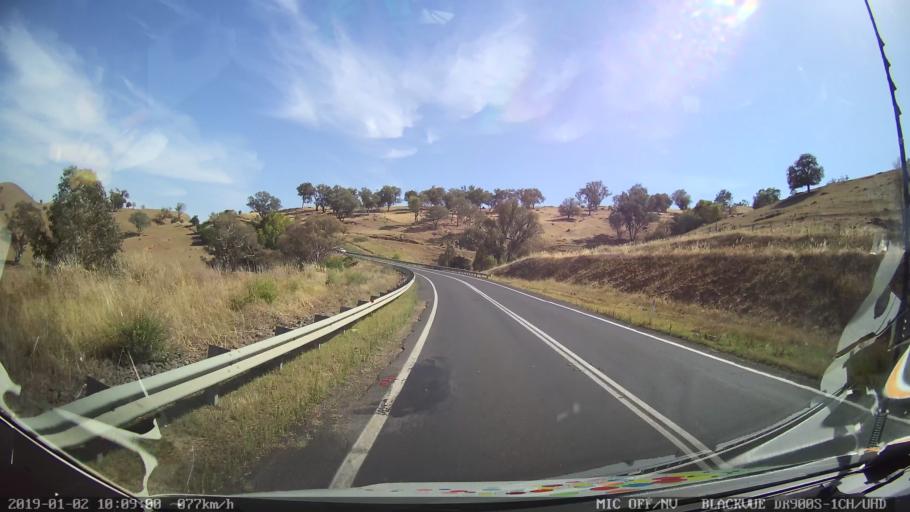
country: AU
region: New South Wales
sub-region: Gundagai
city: Gundagai
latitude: -35.1209
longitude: 148.1008
